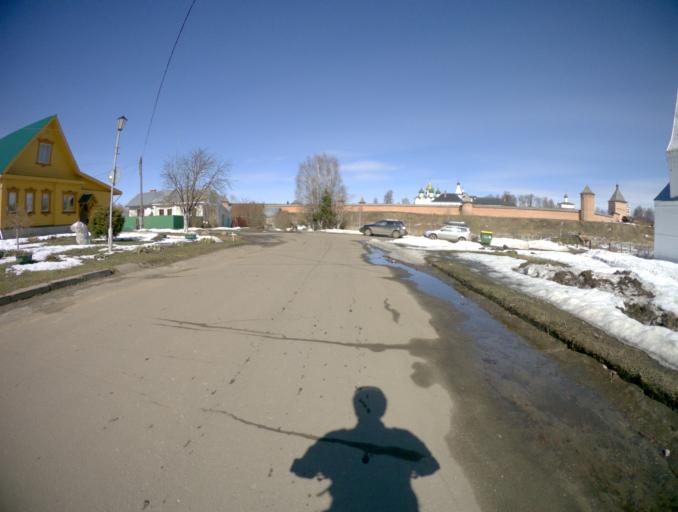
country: RU
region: Vladimir
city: Suzdal'
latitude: 56.4306
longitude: 40.4366
